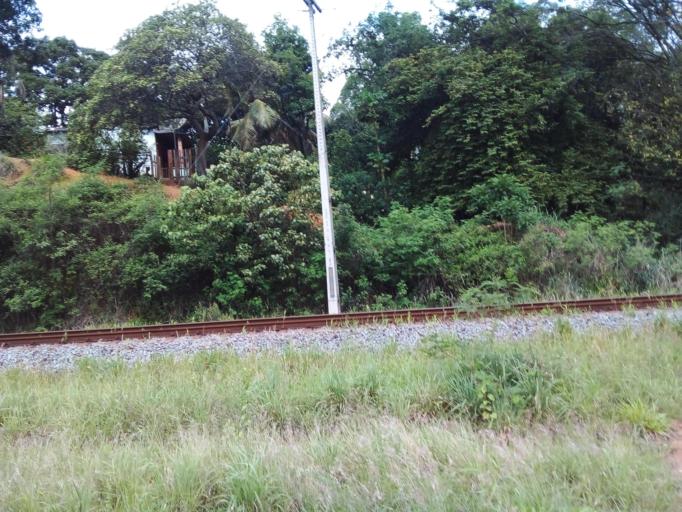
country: BR
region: Espirito Santo
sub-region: Joao Neiva
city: Joao Neiva
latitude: -19.7637
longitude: -40.3689
